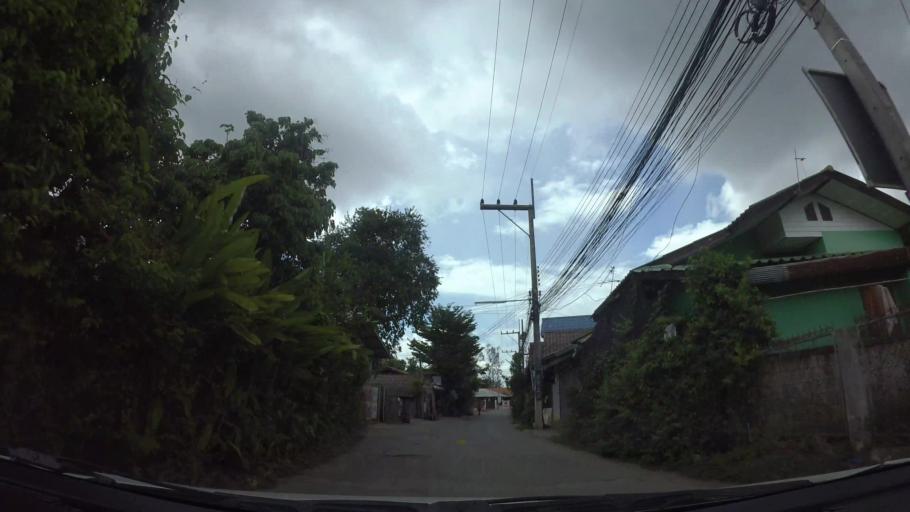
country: TH
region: Chiang Mai
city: Saraphi
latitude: 18.7490
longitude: 99.0392
